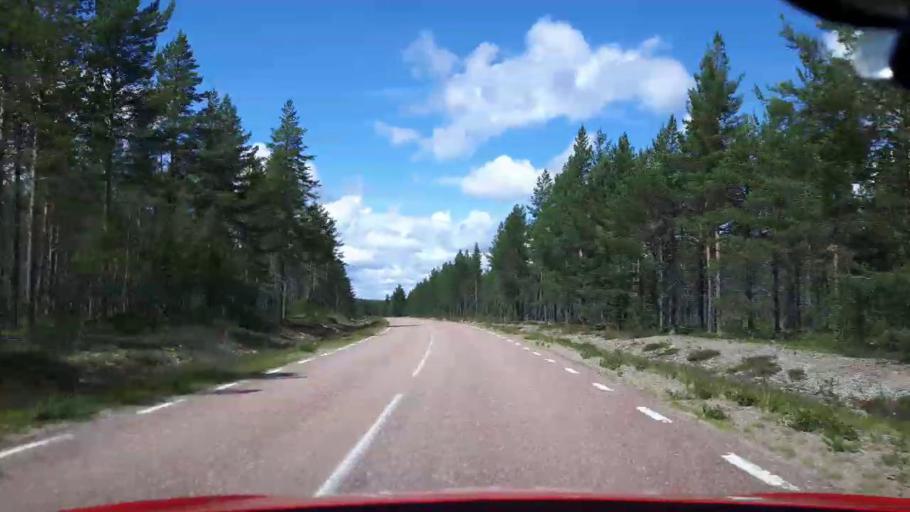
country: SE
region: Dalarna
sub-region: Alvdalens Kommun
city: AElvdalen
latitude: 61.8190
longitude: 13.5804
